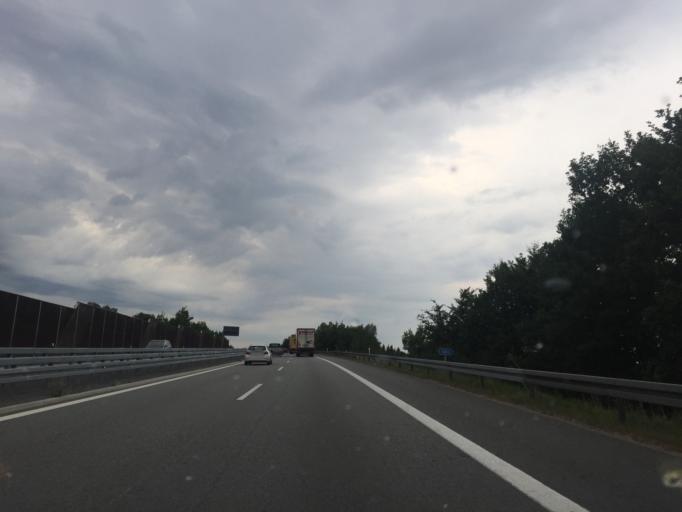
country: DE
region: Bavaria
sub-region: Upper Palatinate
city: Schirmitz
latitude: 49.6523
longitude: 12.1477
